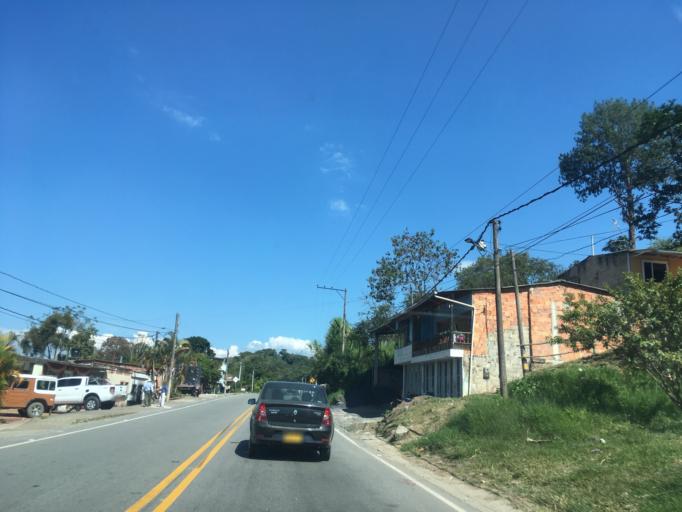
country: CO
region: Santander
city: Suaita
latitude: 6.0696
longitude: -73.4120
